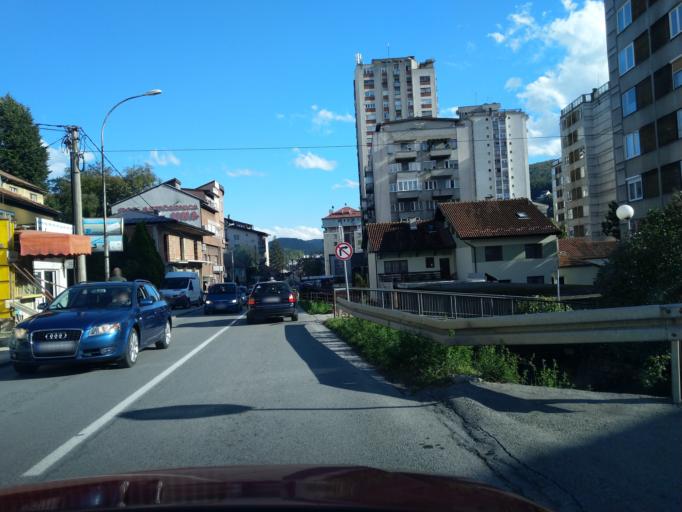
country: RS
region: Central Serbia
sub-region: Zlatiborski Okrug
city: Uzice
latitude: 43.8575
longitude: 19.8334
